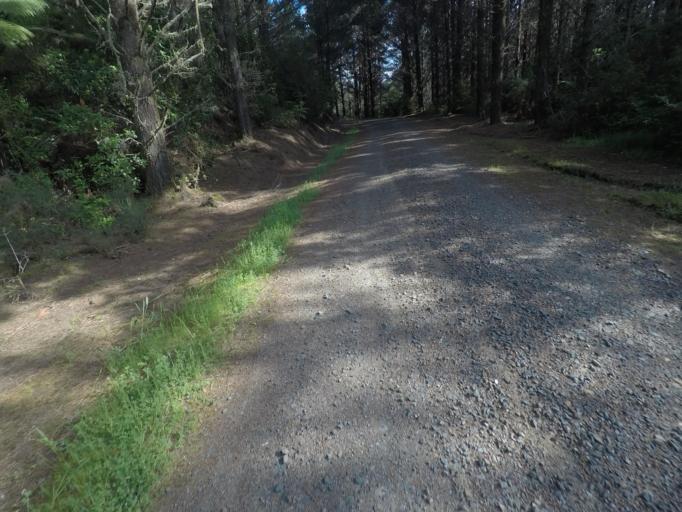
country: NZ
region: Auckland
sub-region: Auckland
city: Muriwai Beach
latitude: -36.7431
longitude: 174.5759
